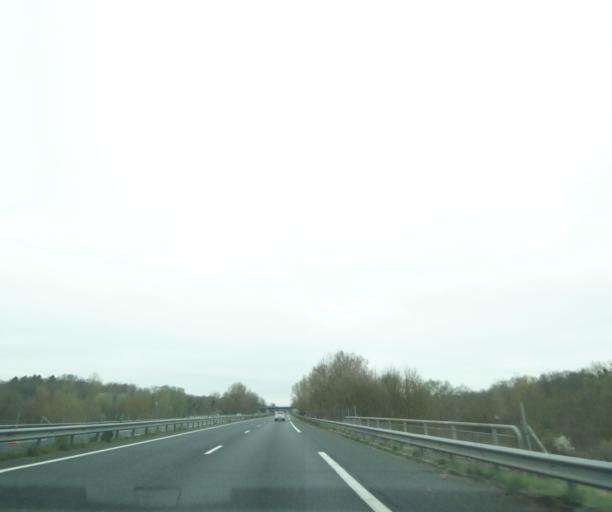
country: FR
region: Centre
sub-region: Departement du Cher
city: Vierzon
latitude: 47.2195
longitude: 2.0404
